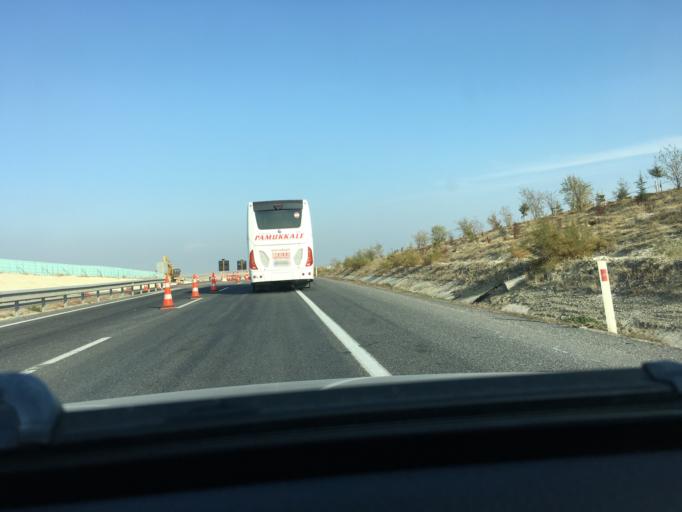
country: TR
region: Eskisehir
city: Gunyuzu
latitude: 39.5705
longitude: 31.8302
